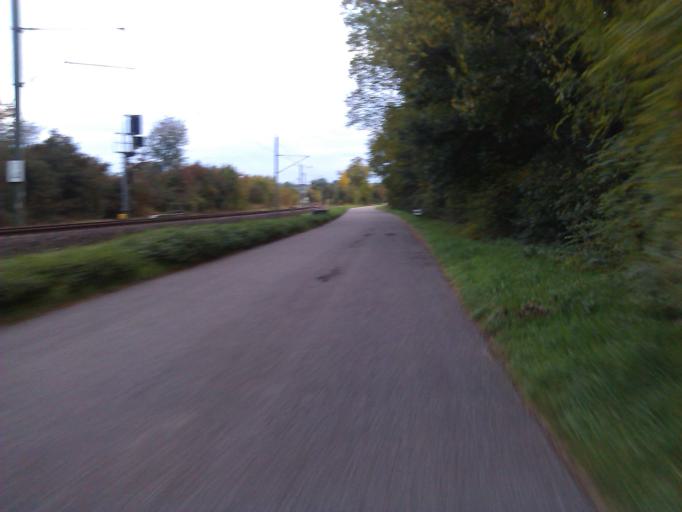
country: DE
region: Baden-Wuerttemberg
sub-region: Karlsruhe Region
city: Meckesheim
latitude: 49.3091
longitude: 8.8137
